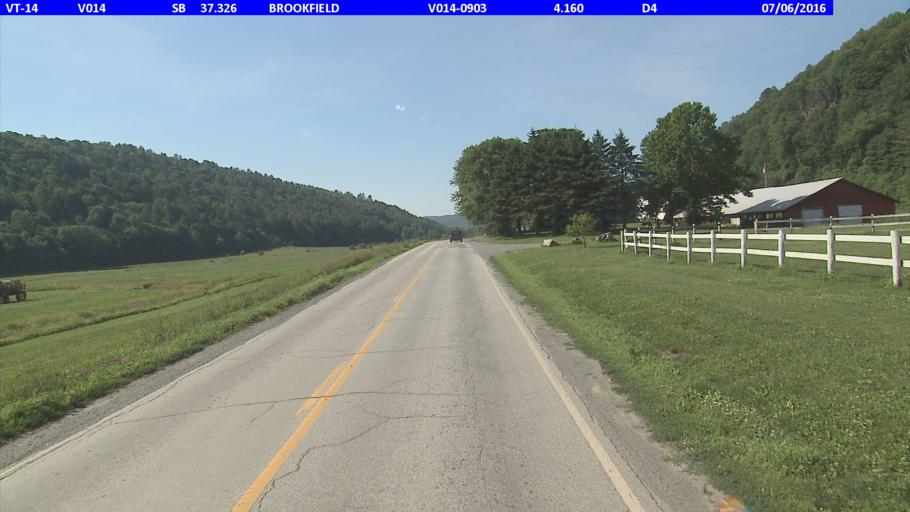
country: US
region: Vermont
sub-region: Orange County
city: Williamstown
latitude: 44.0370
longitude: -72.5692
